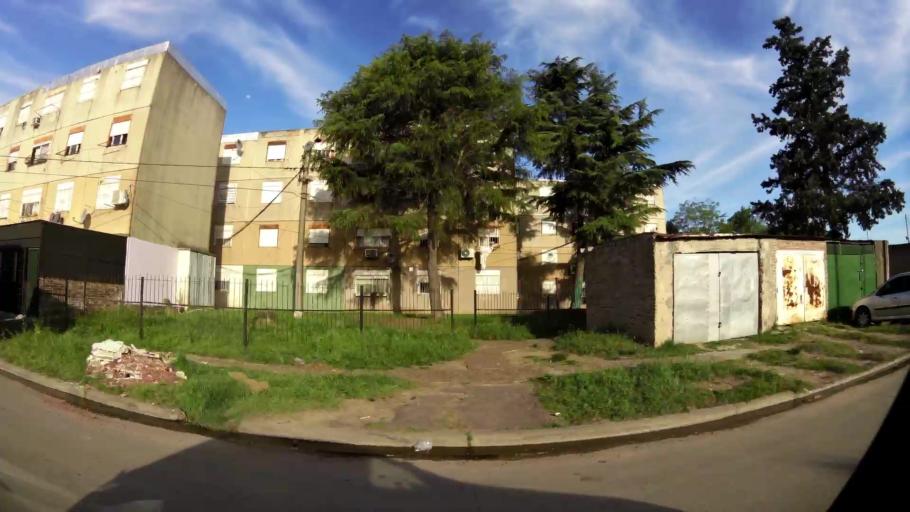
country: AR
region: Buenos Aires
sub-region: Partido de Almirante Brown
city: Adrogue
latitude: -34.8171
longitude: -58.3351
